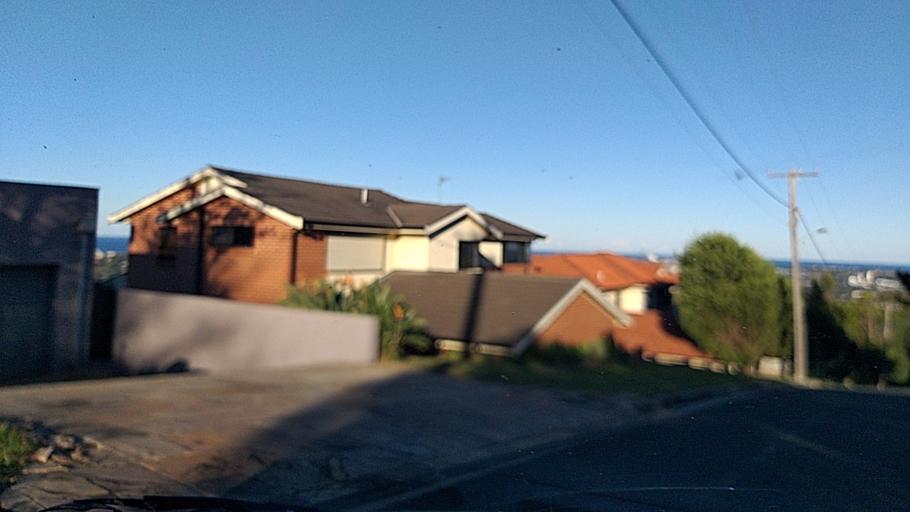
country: AU
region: New South Wales
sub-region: Wollongong
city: Mount Keira
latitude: -34.4241
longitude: 150.8417
